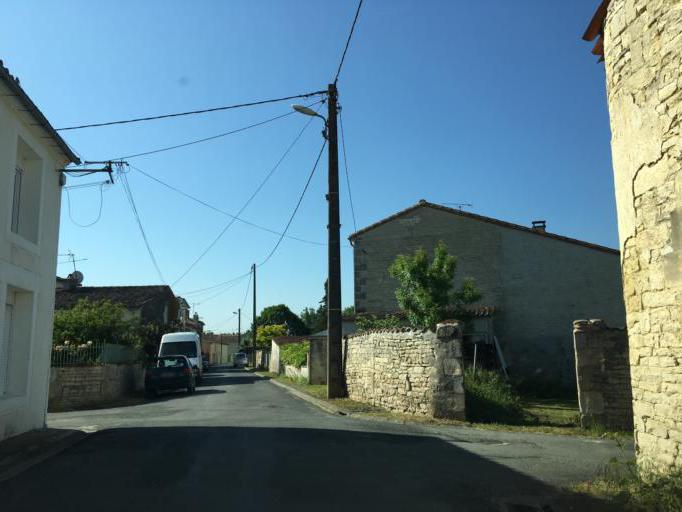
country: FR
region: Poitou-Charentes
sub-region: Departement des Deux-Sevres
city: Beauvoir-sur-Niort
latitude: 46.0972
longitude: -0.5072
